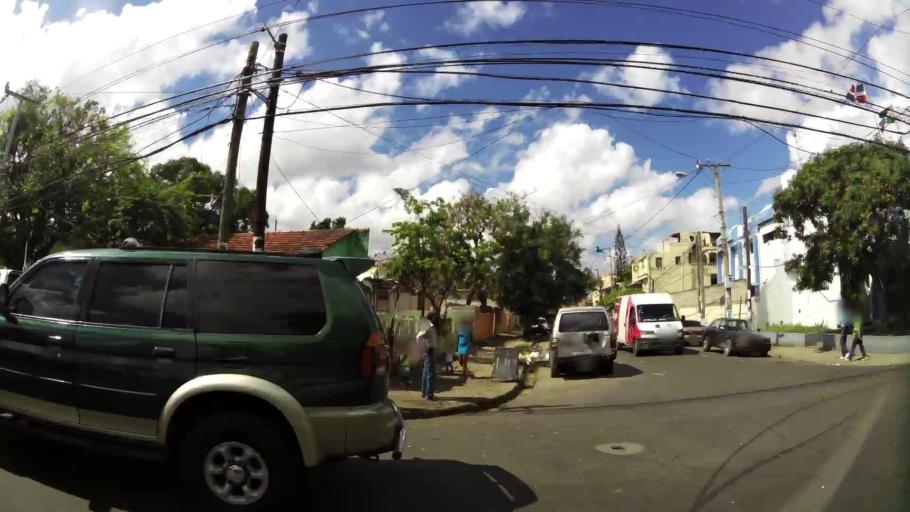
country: DO
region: Nacional
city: San Carlos
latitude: 18.4913
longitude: -69.8865
